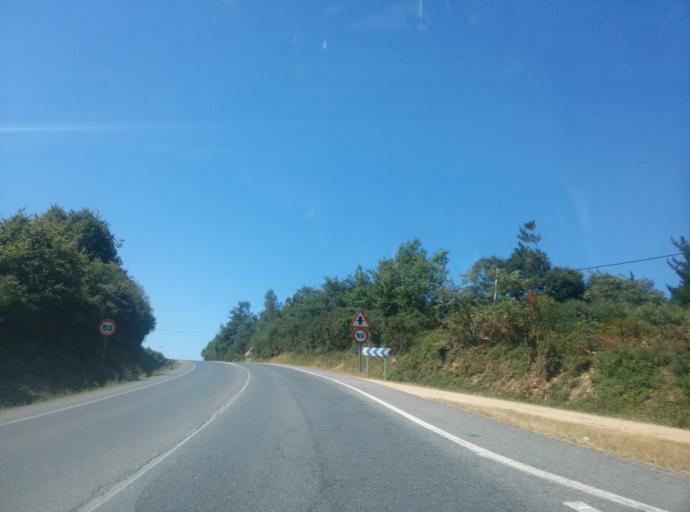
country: ES
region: Galicia
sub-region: Provincia de Lugo
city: Mos
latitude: 43.1253
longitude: -7.4861
